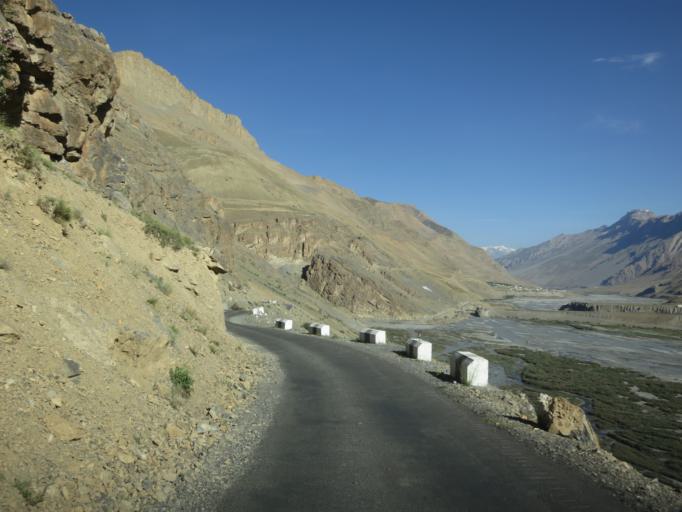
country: IN
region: Himachal Pradesh
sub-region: Shimla
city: Sarahan
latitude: 32.2575
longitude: 78.0432
